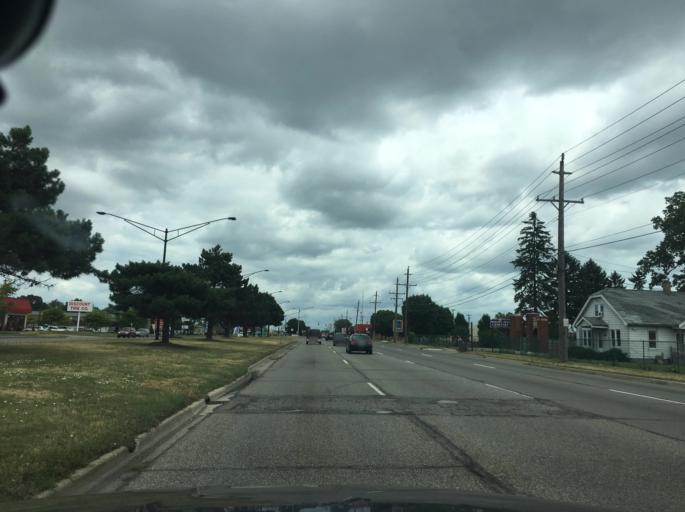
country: US
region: Michigan
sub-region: Macomb County
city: Fraser
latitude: 42.5425
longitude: -82.9070
